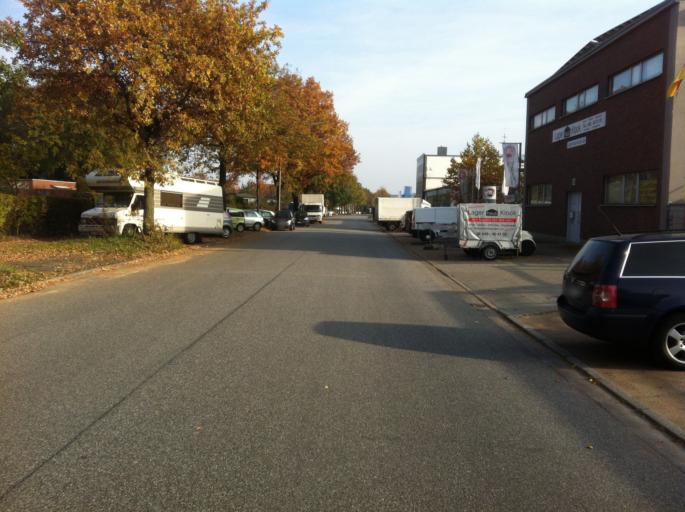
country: DE
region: Hamburg
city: Altona
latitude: 53.5689
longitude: 9.9351
